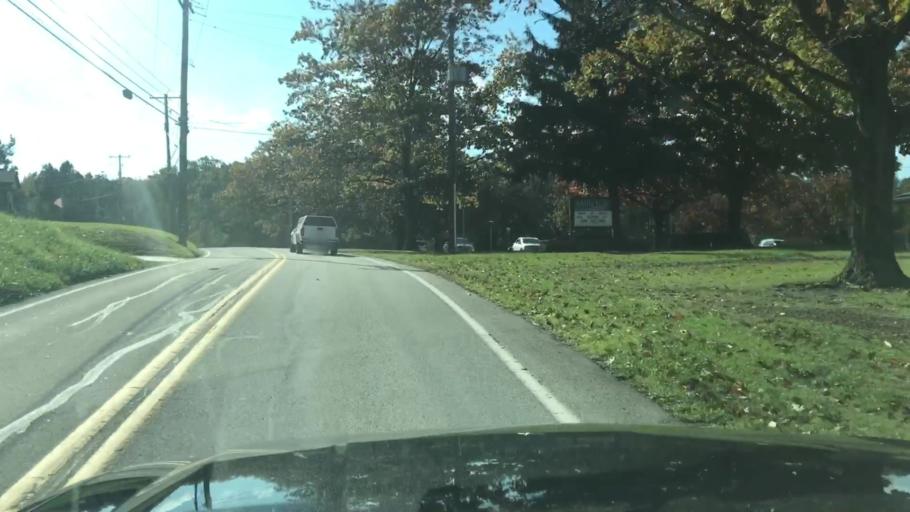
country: US
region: Pennsylvania
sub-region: Cumberland County
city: Lower Allen
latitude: 40.1902
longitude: -76.8901
